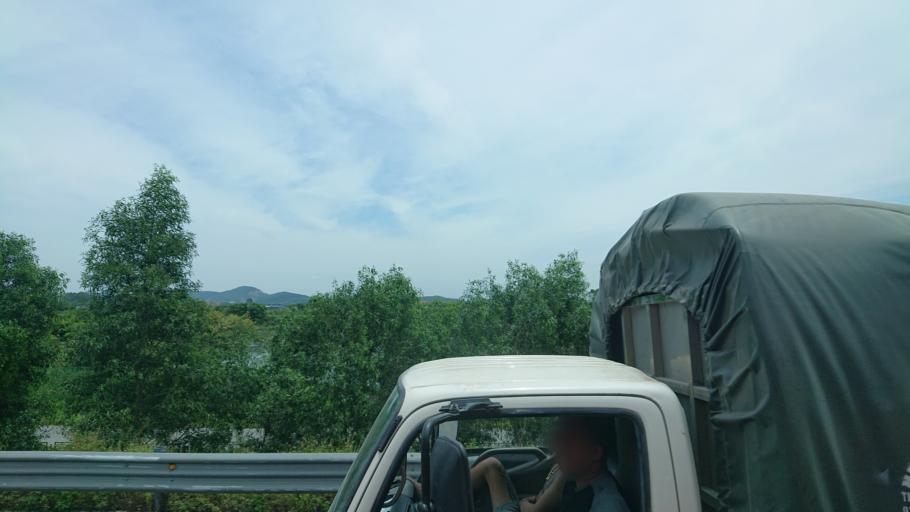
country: VN
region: Hai Phong
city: Tien Lang
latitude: 20.7716
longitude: 106.5859
